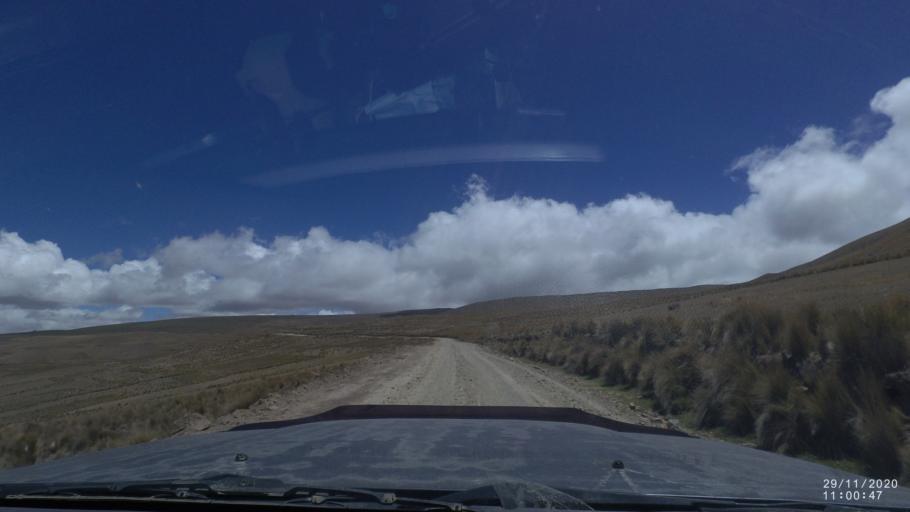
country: BO
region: Cochabamba
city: Cochabamba
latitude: -17.2022
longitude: -66.2246
